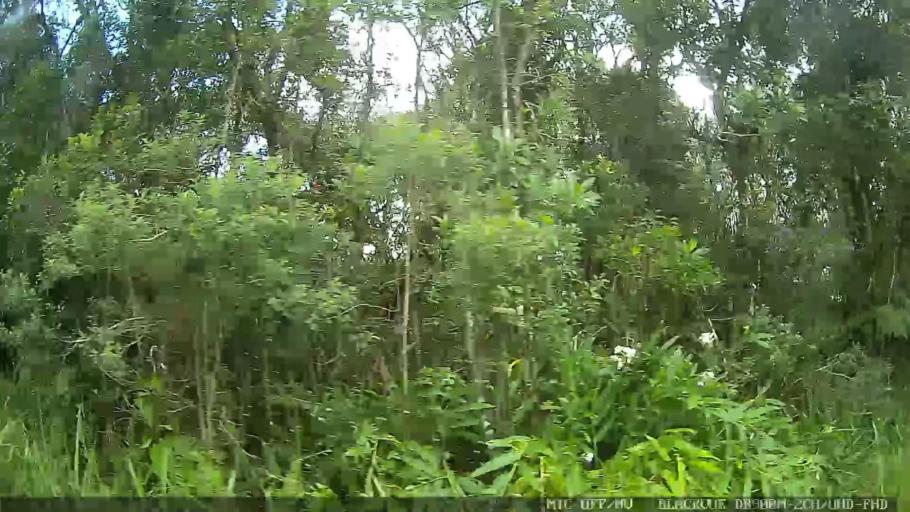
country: BR
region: Sao Paulo
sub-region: Itanhaem
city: Itanhaem
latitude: -24.1854
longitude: -46.9126
